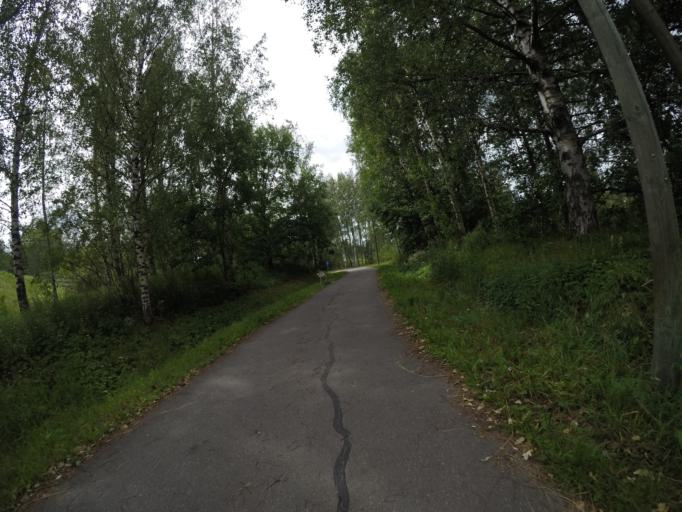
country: FI
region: Haeme
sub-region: Haemeenlinna
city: Haemeenlinna
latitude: 60.9993
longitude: 24.4988
